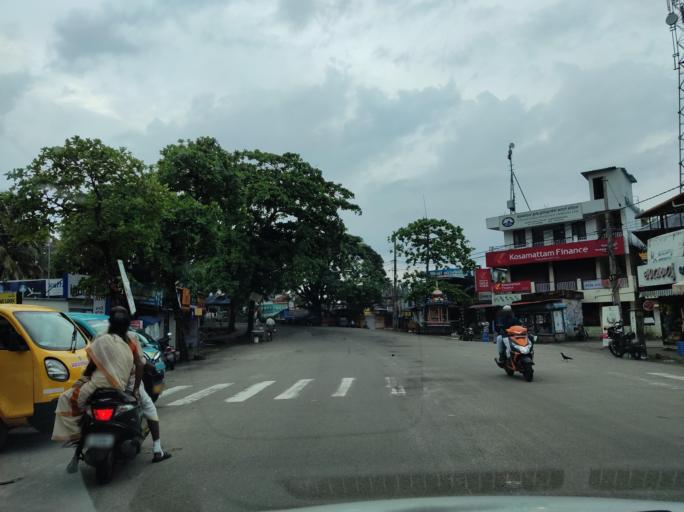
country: IN
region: Kerala
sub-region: Alappuzha
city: Kayankulam
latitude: 9.2589
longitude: 76.4108
